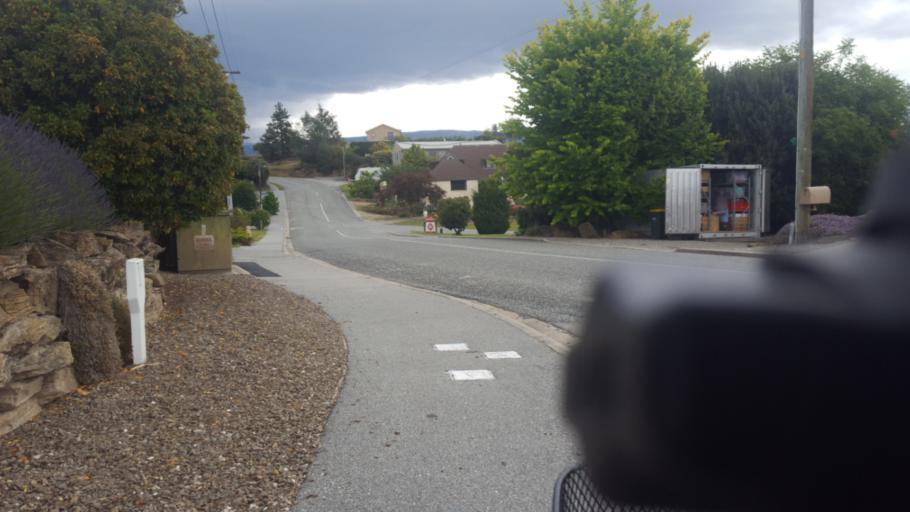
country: NZ
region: Otago
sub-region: Queenstown-Lakes District
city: Wanaka
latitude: -45.2627
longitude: 169.3784
